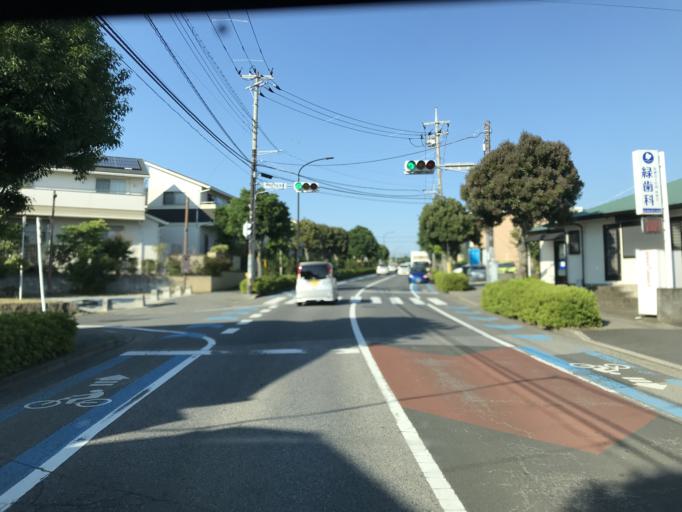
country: JP
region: Chiba
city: Chiba
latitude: 35.5515
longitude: 140.1897
